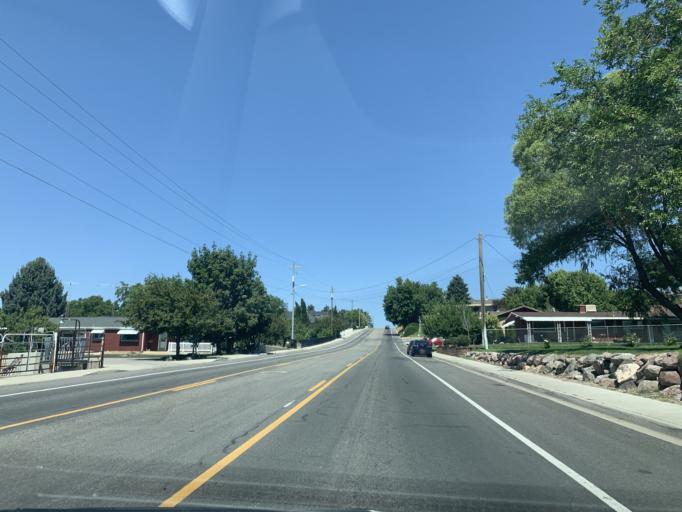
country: US
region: Utah
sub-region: Utah County
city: Lehi
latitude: 40.4025
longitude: -111.8302
